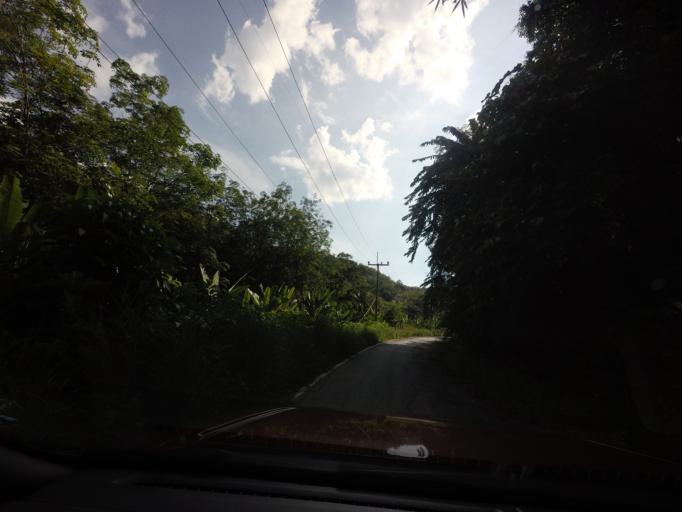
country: TH
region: Yala
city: Than To
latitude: 6.0641
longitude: 101.3623
